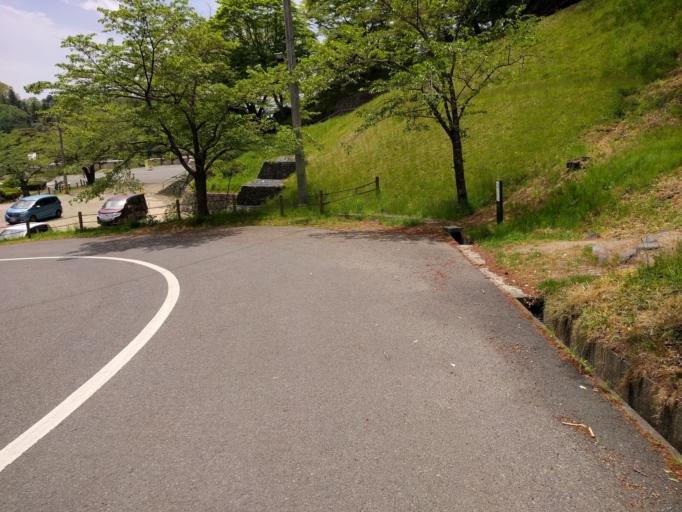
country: JP
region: Fukushima
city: Nihommatsu
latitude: 37.5985
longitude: 140.4310
